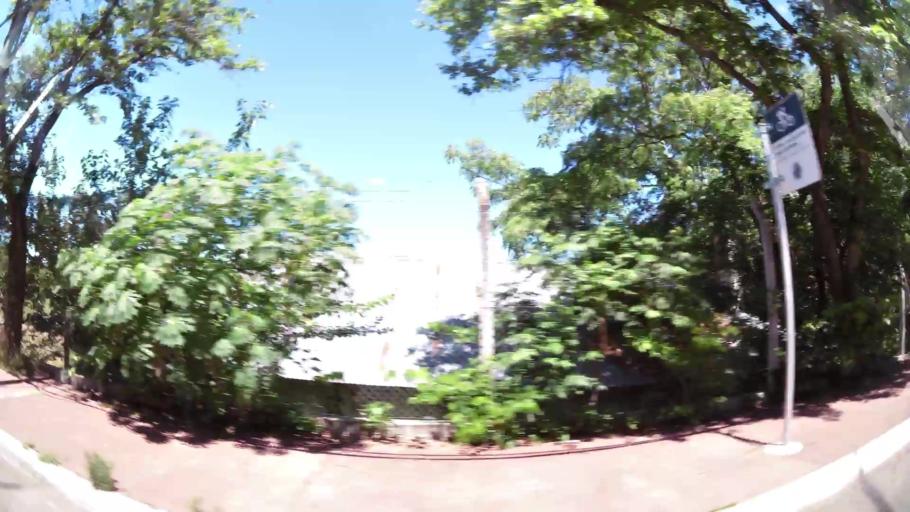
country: AR
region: Buenos Aires
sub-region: Partido de San Isidro
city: San Isidro
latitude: -34.4531
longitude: -58.5225
